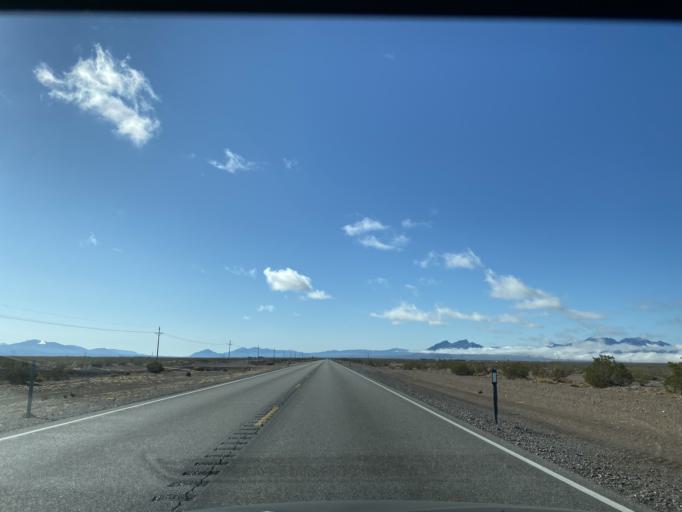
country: US
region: Nevada
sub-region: Nye County
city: Beatty
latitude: 36.5517
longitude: -116.4166
